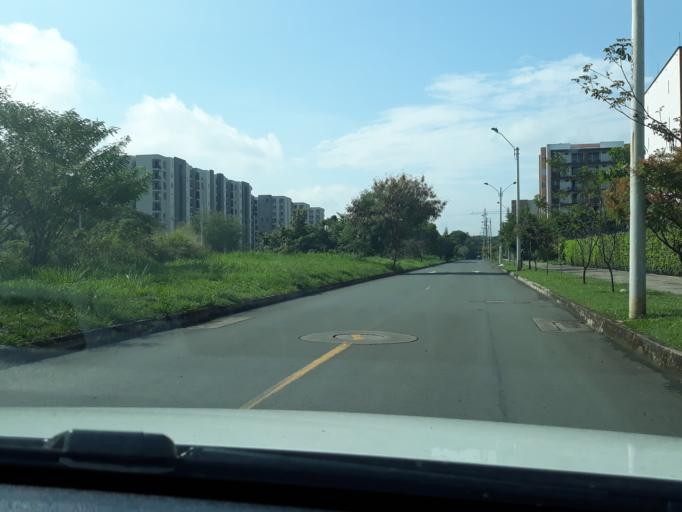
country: CO
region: Valle del Cauca
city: Cali
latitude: 3.3582
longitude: -76.5163
